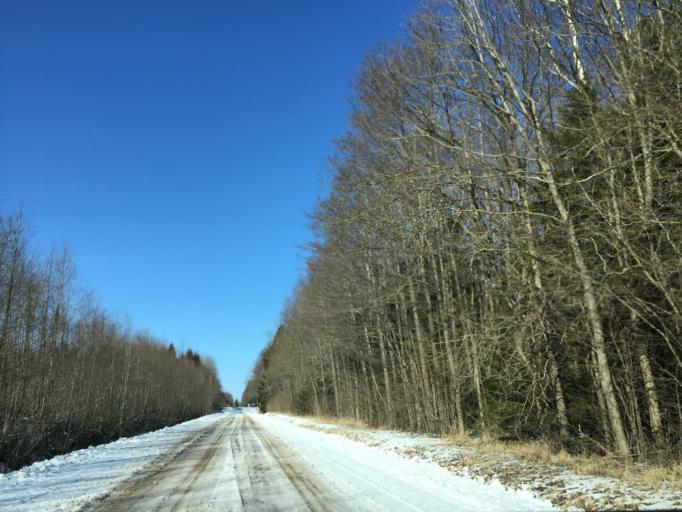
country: LV
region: Salacgrivas
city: Ainazi
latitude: 58.0303
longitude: 24.5118
